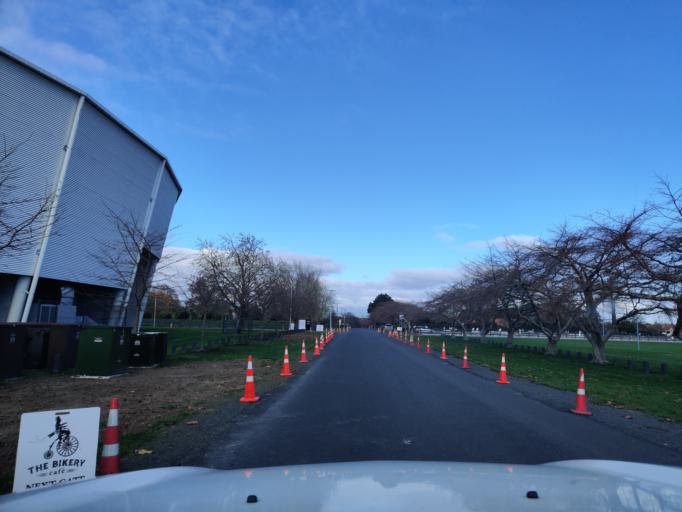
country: NZ
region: Waikato
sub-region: Waipa District
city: Cambridge
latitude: -37.8900
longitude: 175.4344
